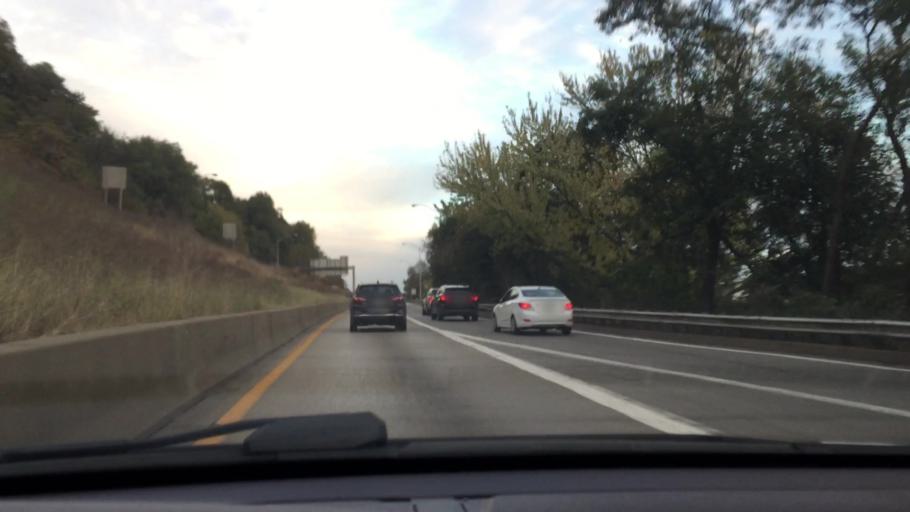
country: US
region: Pennsylvania
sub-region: Allegheny County
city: Aspinwall
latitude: 40.4950
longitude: -79.9073
